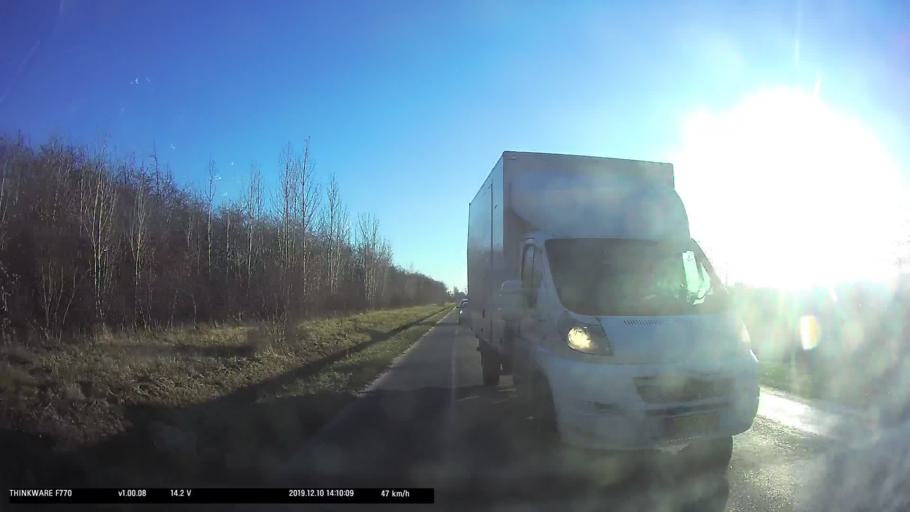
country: DK
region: Capital Region
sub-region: Tarnby Kommune
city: Tarnby
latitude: 55.5711
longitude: 12.5820
